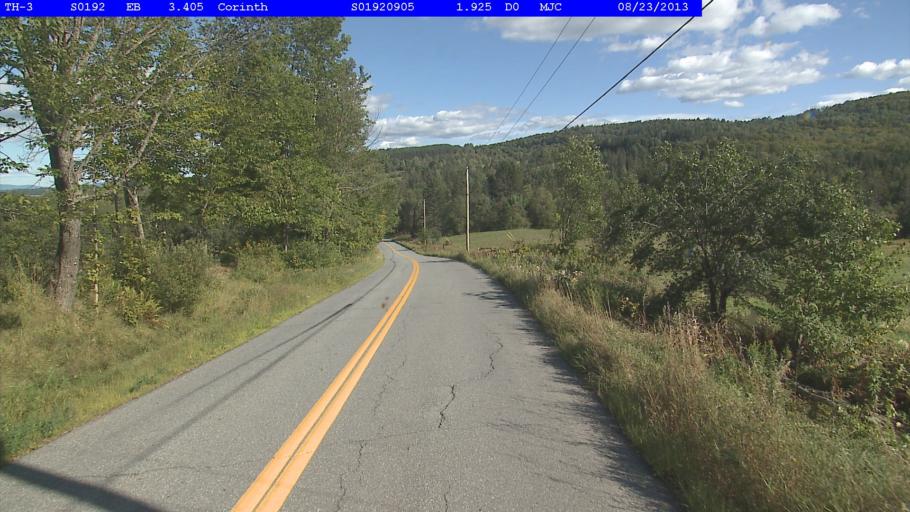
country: US
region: Vermont
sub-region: Orange County
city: Chelsea
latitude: 44.0027
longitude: -72.3211
